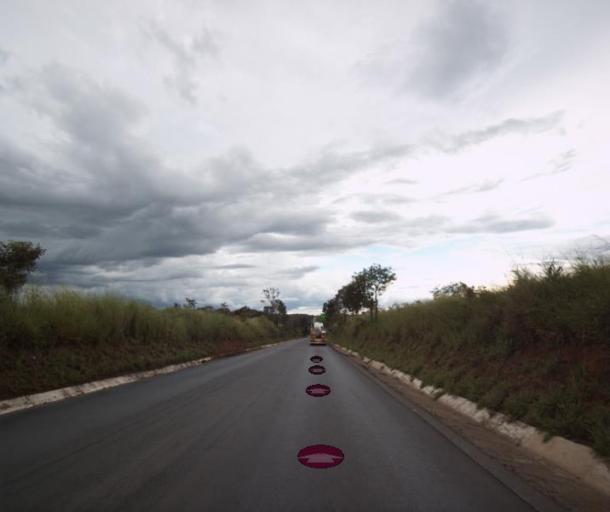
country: BR
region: Goias
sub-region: Itapaci
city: Itapaci
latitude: -15.0079
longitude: -49.4162
